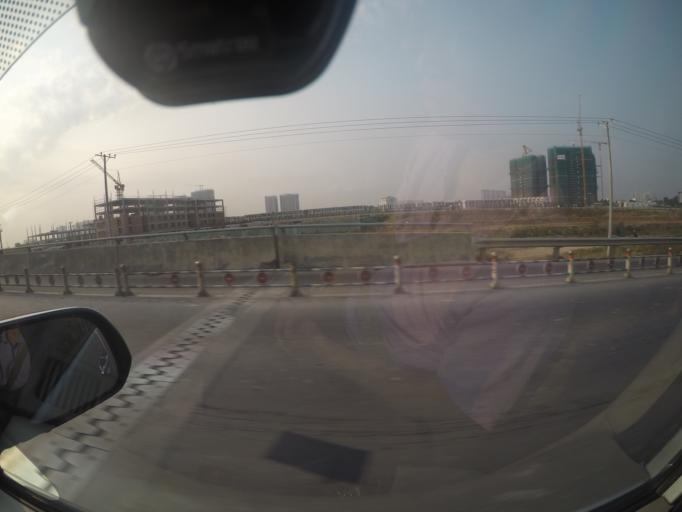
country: VN
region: Ho Chi Minh City
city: Quan Hai
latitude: 10.7954
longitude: 106.7626
